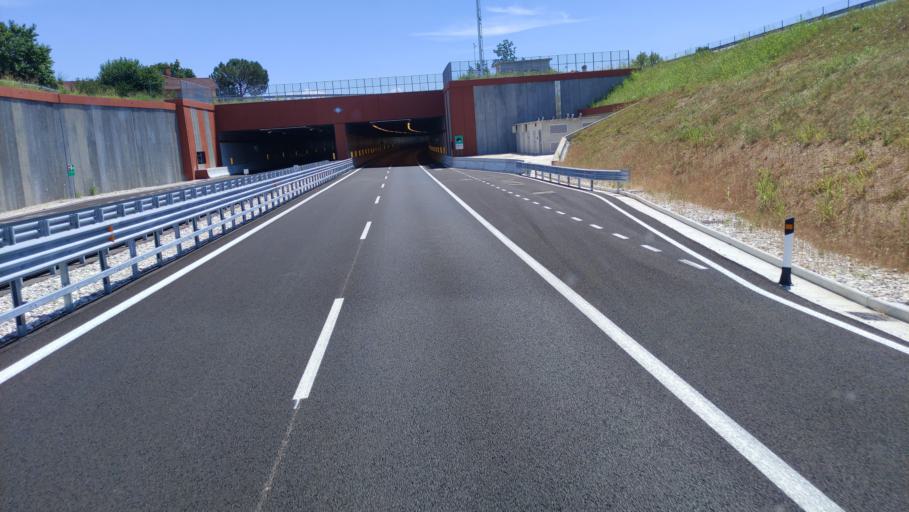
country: IT
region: Veneto
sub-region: Provincia di Treviso
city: San Vito
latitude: 45.7496
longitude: 11.9077
